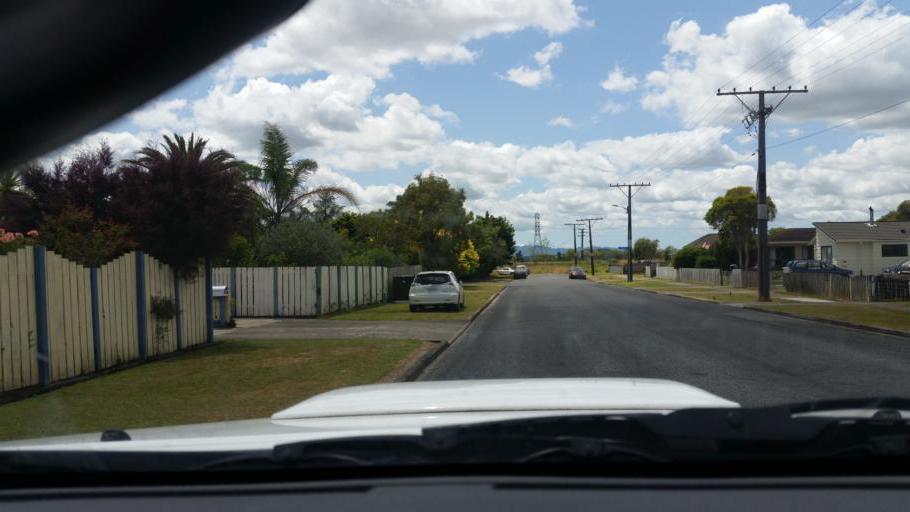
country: NZ
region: Northland
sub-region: Kaipara District
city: Dargaville
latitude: -35.9316
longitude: 173.8747
